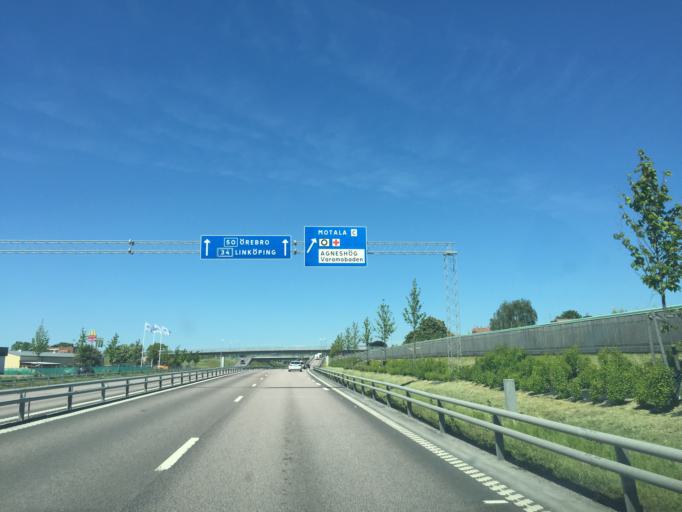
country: SE
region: OEstergoetland
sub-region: Motala Kommun
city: Motala
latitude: 58.5418
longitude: 15.0165
